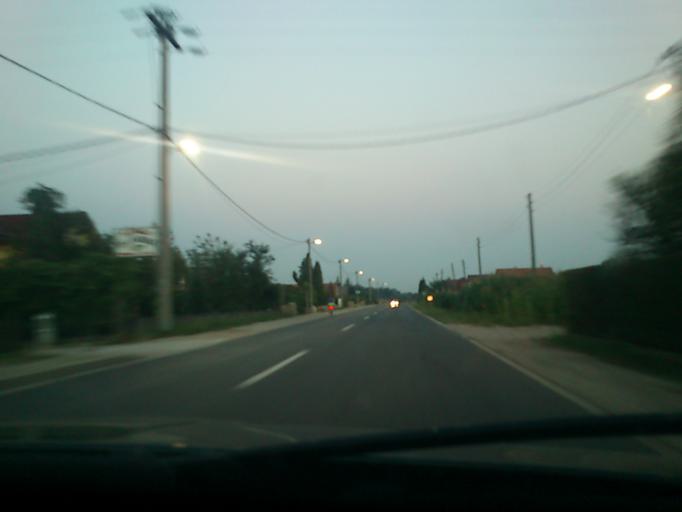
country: SI
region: Starse
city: Starse
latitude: 46.4755
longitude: 15.7490
